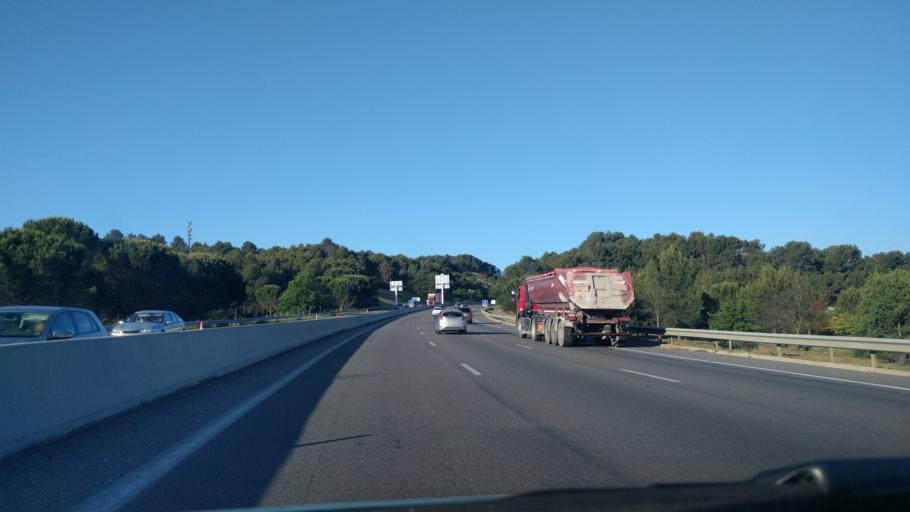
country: FR
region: Provence-Alpes-Cote d'Azur
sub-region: Departement des Bouches-du-Rhone
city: Venelles
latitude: 43.6019
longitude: 5.4961
